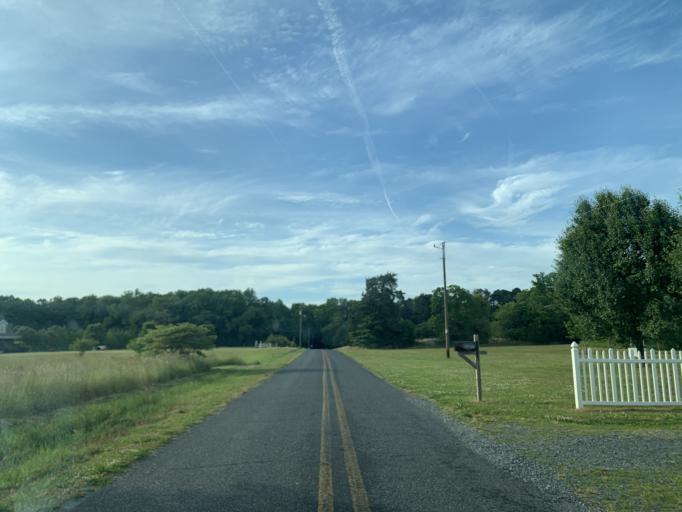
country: US
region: Maryland
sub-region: Worcester County
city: Pocomoke City
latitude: 38.0896
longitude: -75.4641
